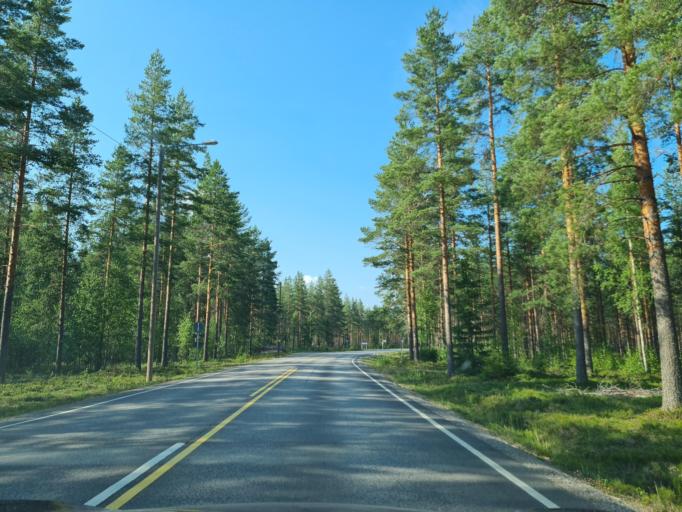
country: FI
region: Satakunta
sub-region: Pohjois-Satakunta
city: Karvia
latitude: 62.0727
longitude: 22.5069
